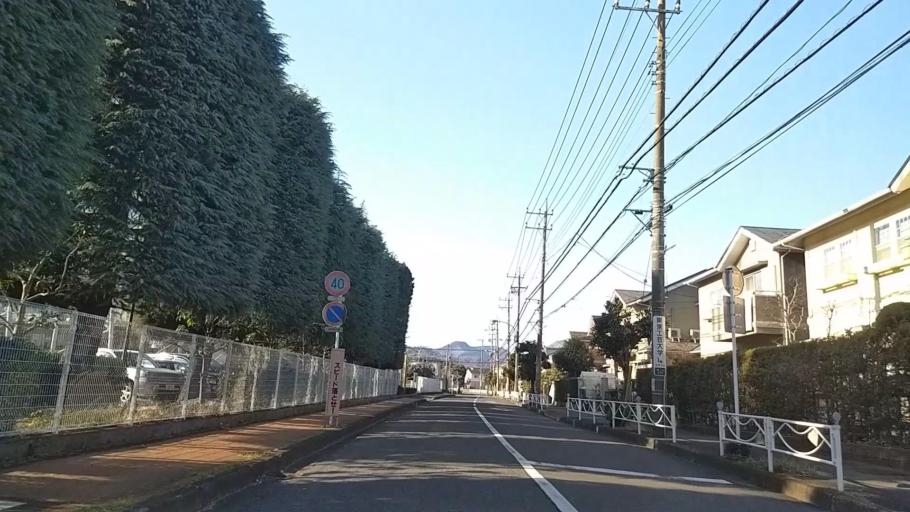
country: JP
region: Kanagawa
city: Atsugi
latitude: 35.4610
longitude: 139.3299
